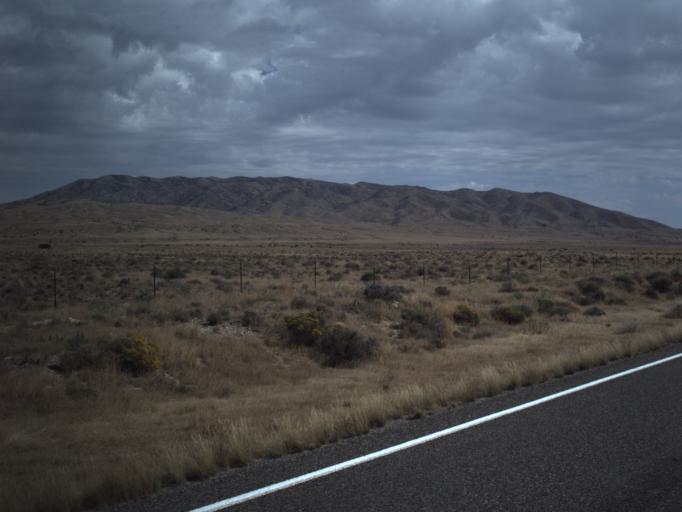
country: US
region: Utah
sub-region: Tooele County
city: Wendover
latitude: 41.4351
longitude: -113.7595
